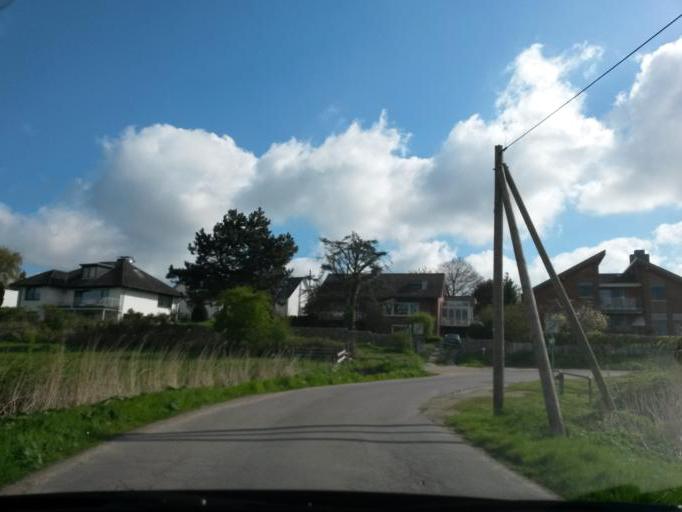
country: DE
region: Schleswig-Holstein
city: Wedel
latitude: 53.5874
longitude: 9.6852
